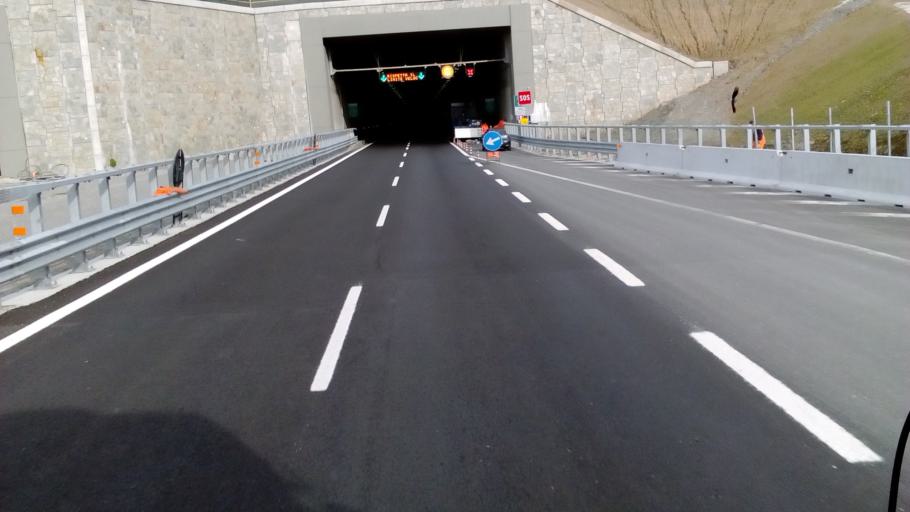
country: IT
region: Tuscany
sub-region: Province of Florence
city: Barberino di Mugello
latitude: 44.0729
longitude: 11.2389
